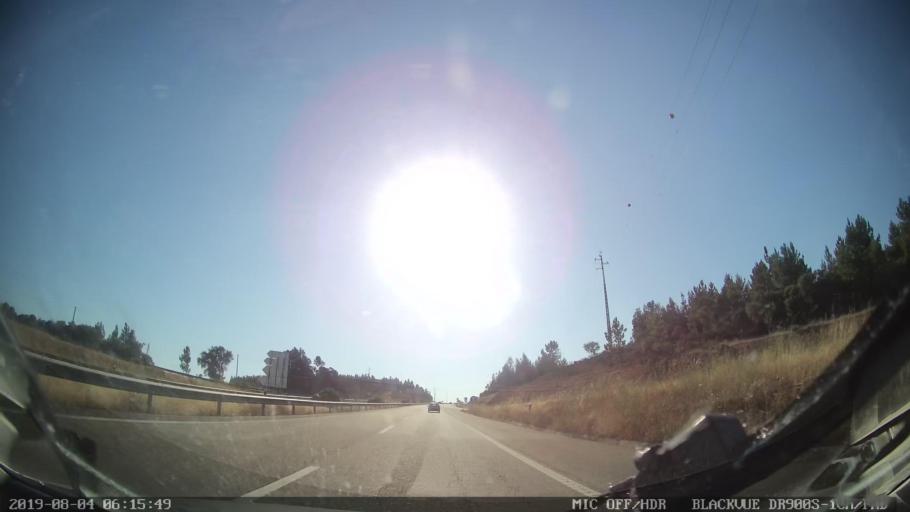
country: PT
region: Santarem
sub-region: Abrantes
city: Tramagal
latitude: 39.4867
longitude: -8.2769
